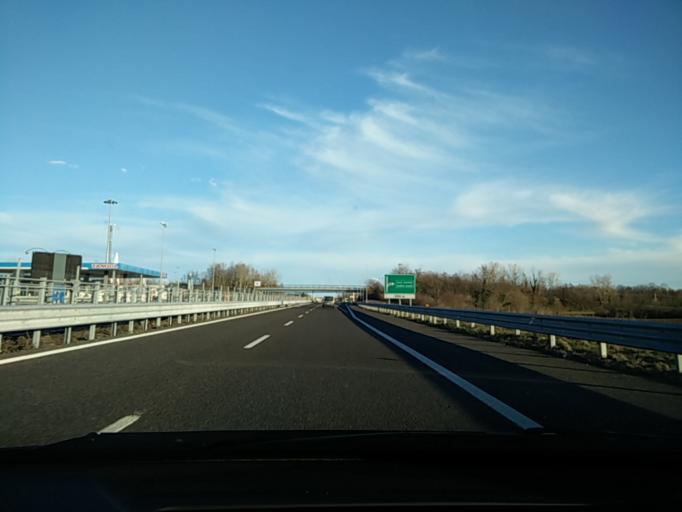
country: IT
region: Friuli Venezia Giulia
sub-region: Provincia di Udine
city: Santo Stefano
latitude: 46.1883
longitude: 13.1147
